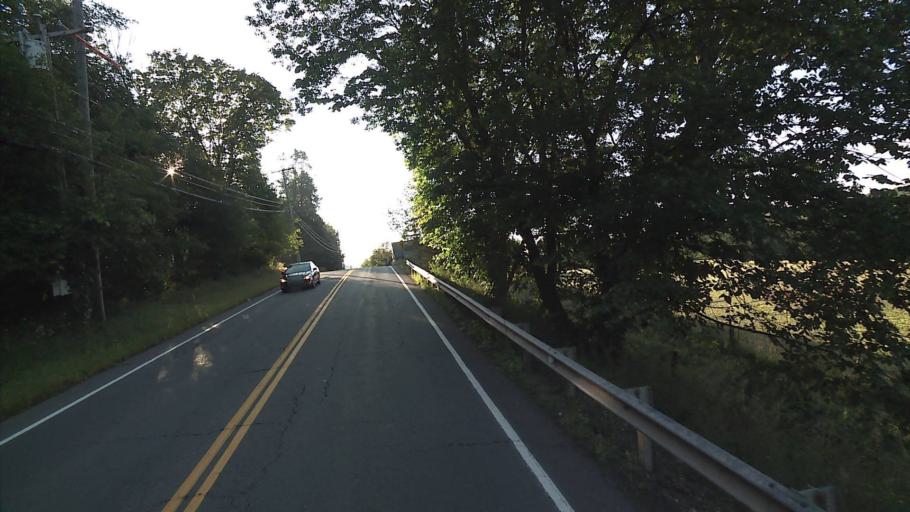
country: US
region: Connecticut
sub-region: Tolland County
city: South Coventry
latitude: 41.7990
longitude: -72.2943
